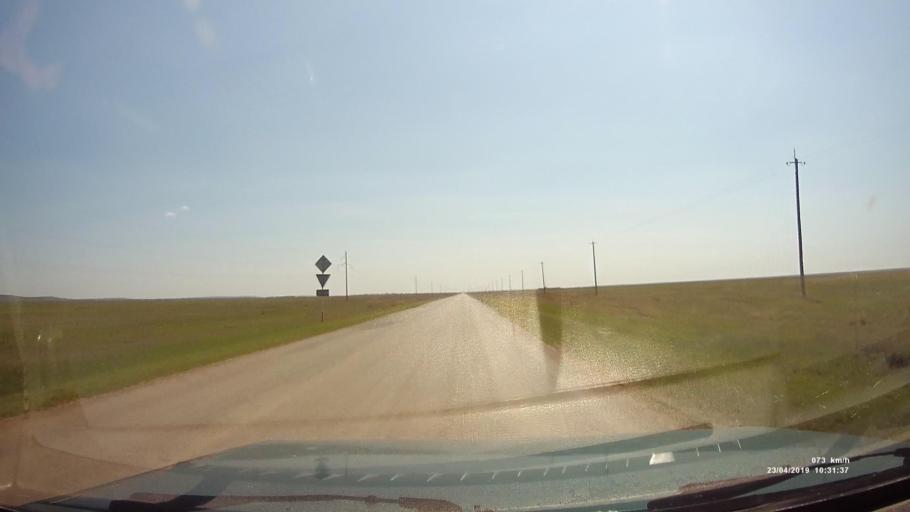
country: RU
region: Kalmykiya
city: Yashalta
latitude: 46.5849
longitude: 42.5647
